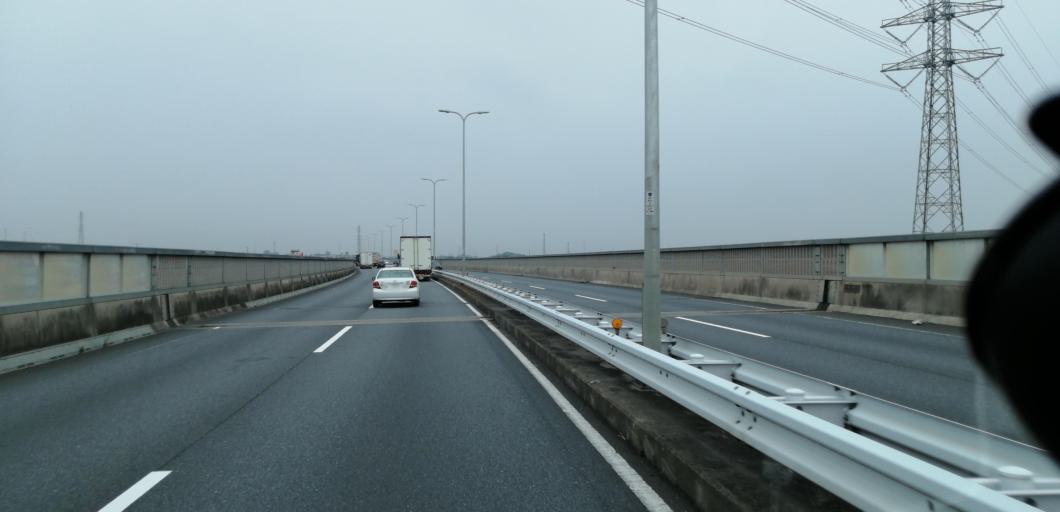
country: JP
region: Saitama
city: Kumagaya
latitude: 36.1650
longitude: 139.3911
